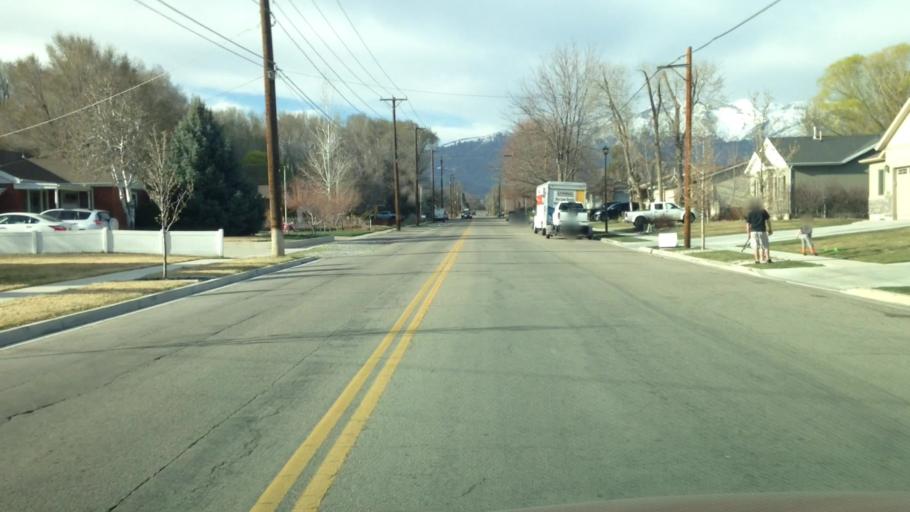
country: US
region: Utah
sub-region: Utah County
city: American Fork
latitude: 40.3892
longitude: -111.7932
